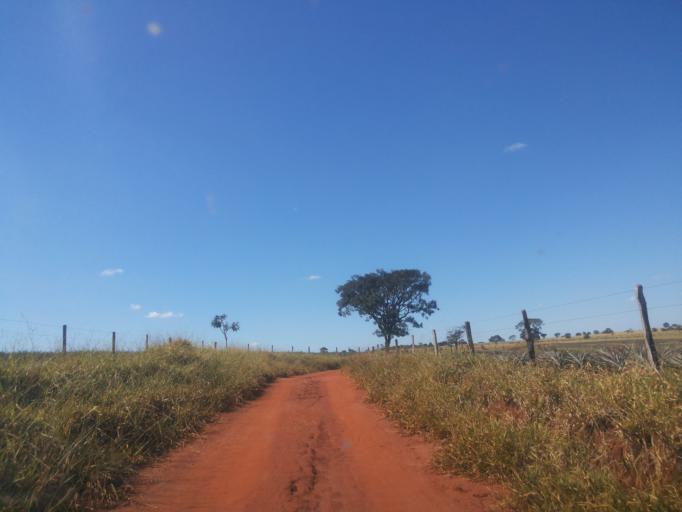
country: BR
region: Minas Gerais
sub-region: Centralina
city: Centralina
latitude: -18.7524
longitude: -49.1823
